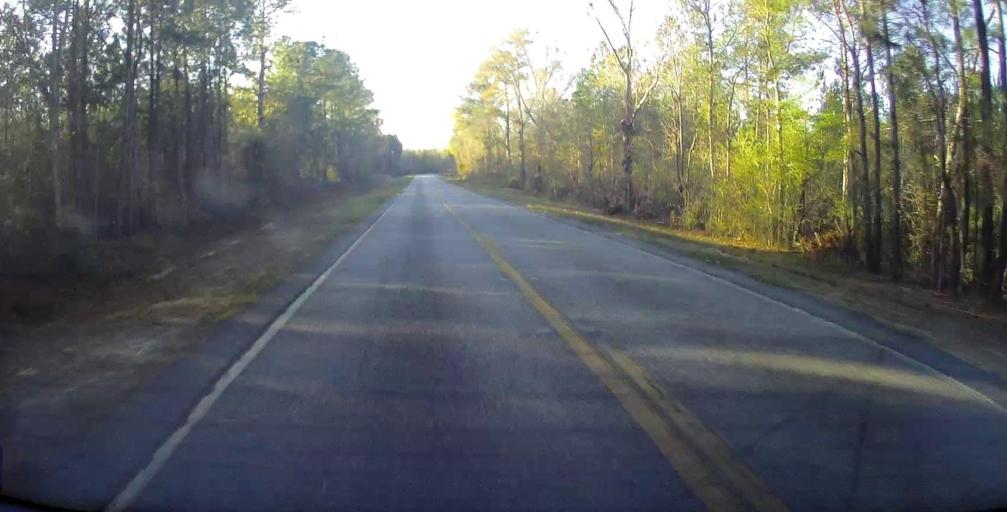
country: US
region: Georgia
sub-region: Wilcox County
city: Abbeville
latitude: 32.0686
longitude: -83.2800
